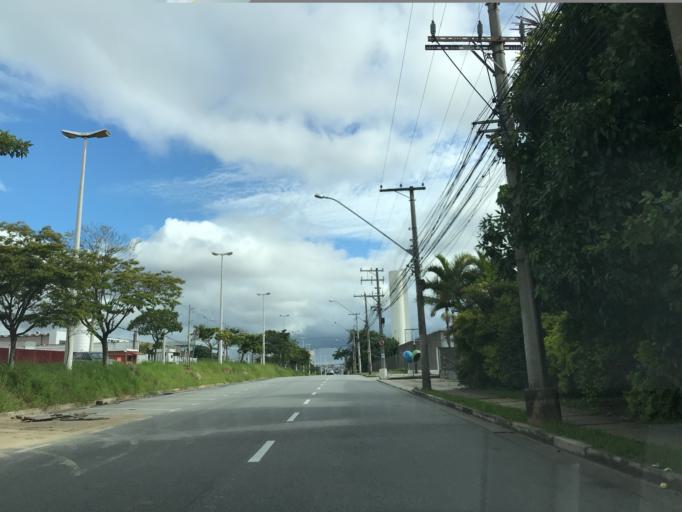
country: BR
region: Sao Paulo
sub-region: Carapicuiba
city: Carapicuiba
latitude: -23.4934
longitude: -46.8354
